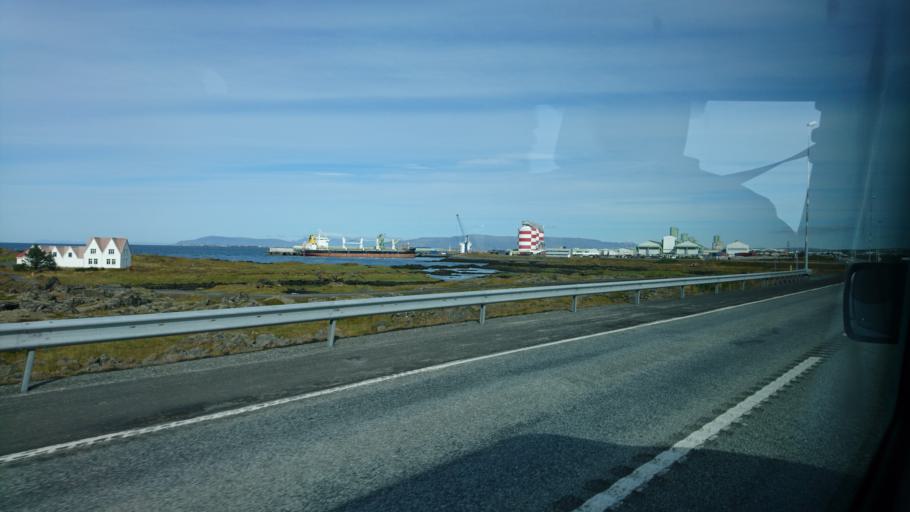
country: IS
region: Capital Region
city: Alftanes
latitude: 64.0395
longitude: -22.0469
